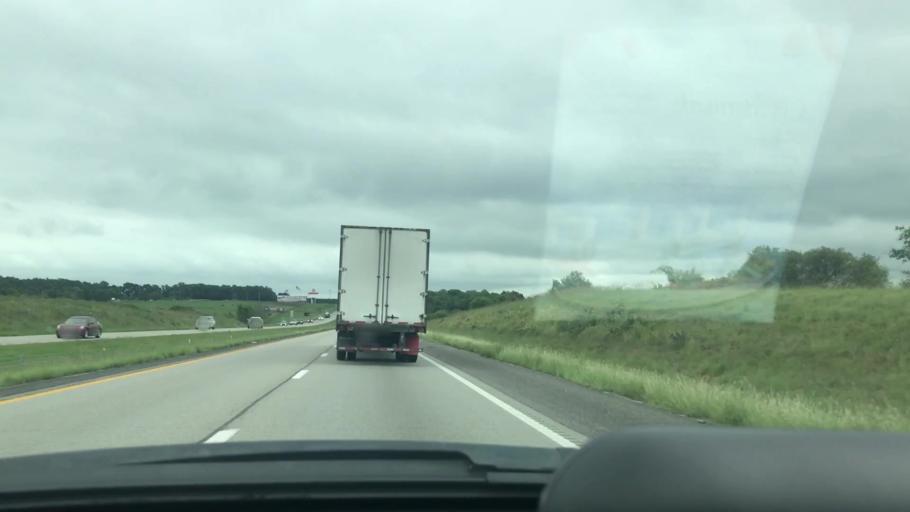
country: US
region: Missouri
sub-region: Christian County
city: Billings
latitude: 37.1859
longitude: -93.5834
